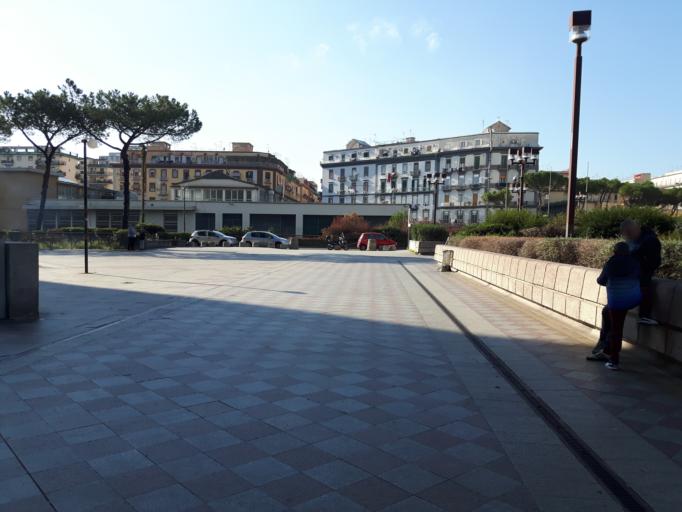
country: IT
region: Campania
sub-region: Provincia di Napoli
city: Napoli
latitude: 40.8563
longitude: 14.2777
